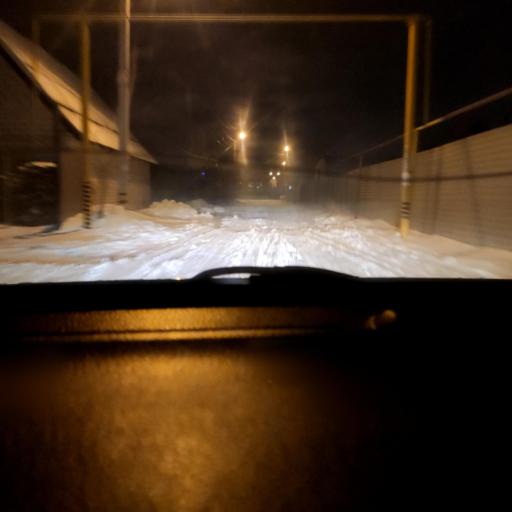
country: RU
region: Voronezj
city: Somovo
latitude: 51.7464
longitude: 39.3306
